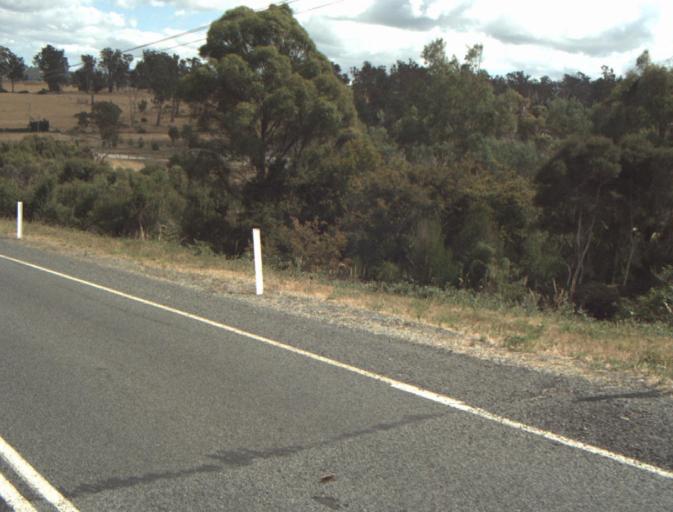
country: AU
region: Tasmania
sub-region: Launceston
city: Mayfield
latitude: -41.3032
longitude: 147.0490
